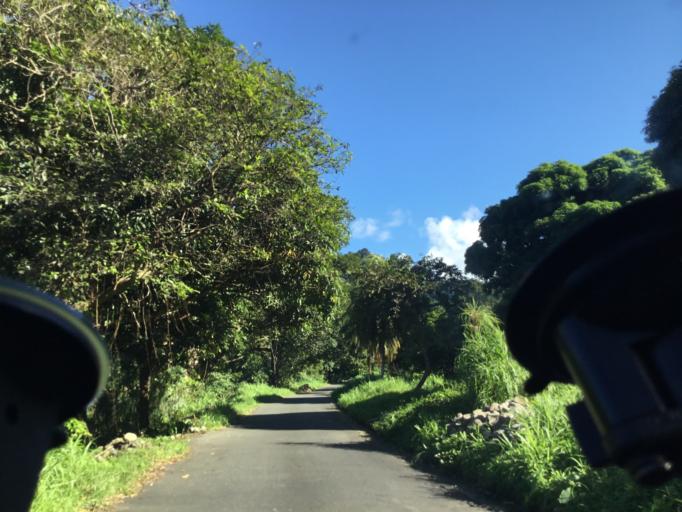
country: VC
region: Saint David
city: Chateaubelair
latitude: 13.3011
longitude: -61.2287
